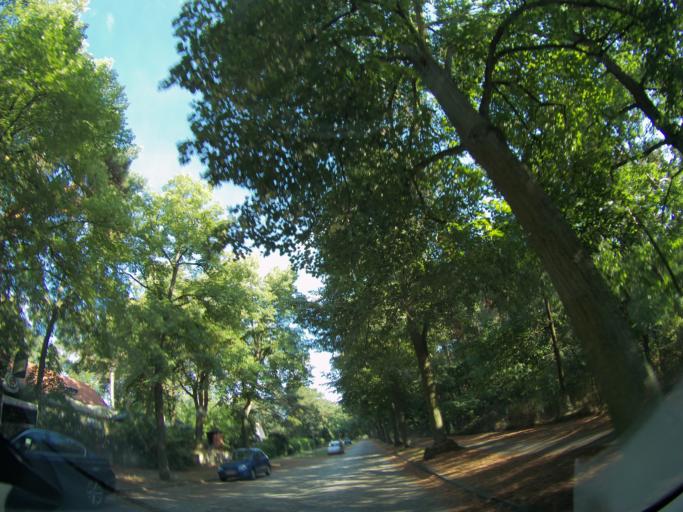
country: DE
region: Brandenburg
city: Stahnsdorf
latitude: 52.3885
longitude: 13.1896
